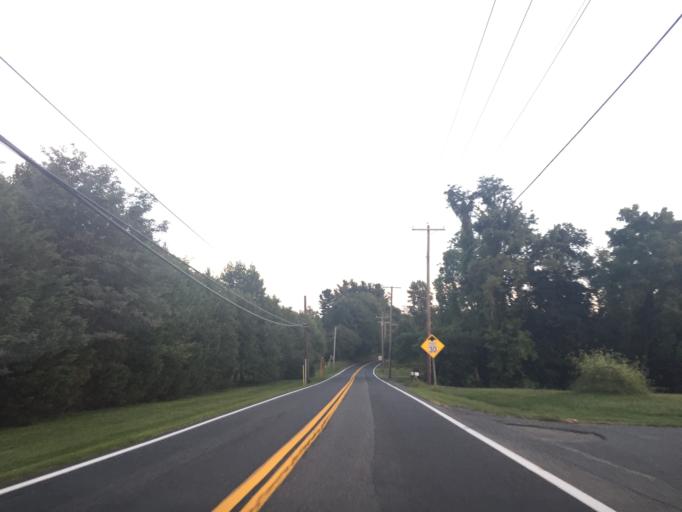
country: US
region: Maryland
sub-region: Harford County
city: Bel Air North
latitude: 39.5927
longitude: -76.3887
